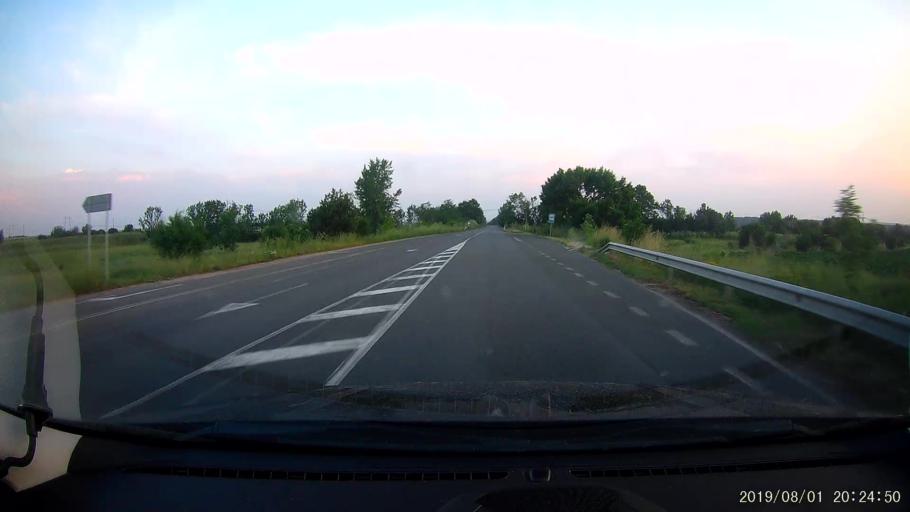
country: BG
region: Yambol
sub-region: Obshtina Elkhovo
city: Elkhovo
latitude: 42.2255
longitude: 26.5912
